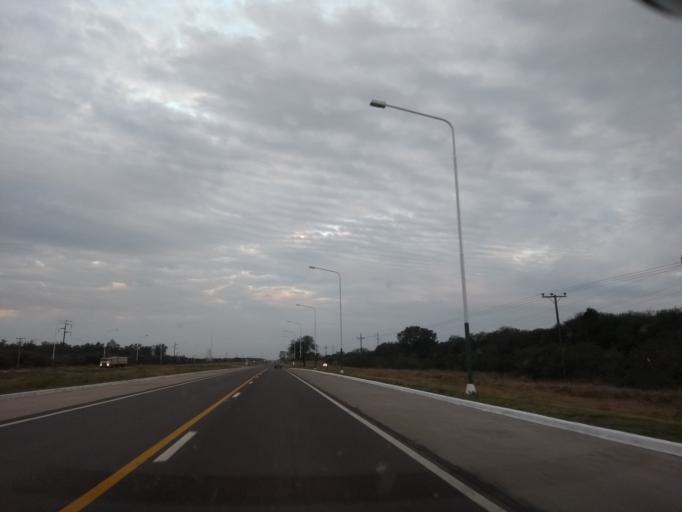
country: AR
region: Chaco
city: Puerto Tirol
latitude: -27.2694
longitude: -59.1457
